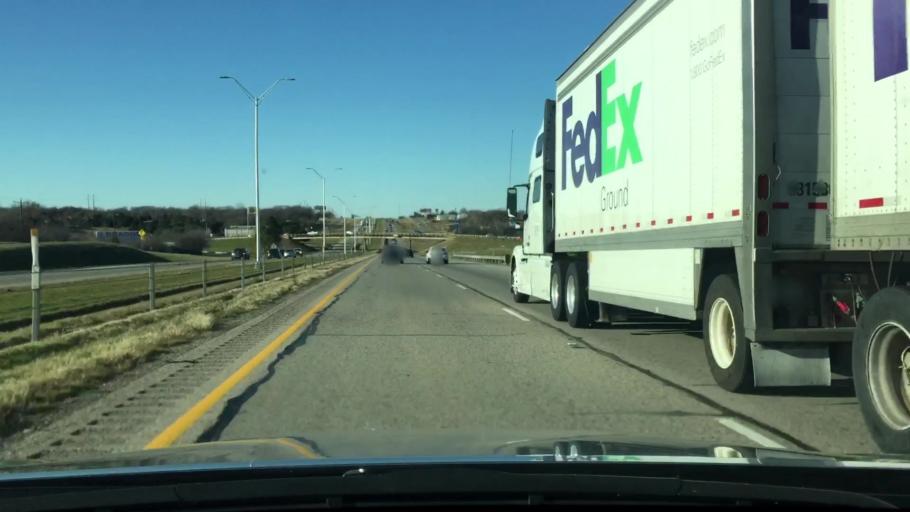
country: US
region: Texas
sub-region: Johnson County
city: Alvarado
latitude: 32.4619
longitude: -97.2644
